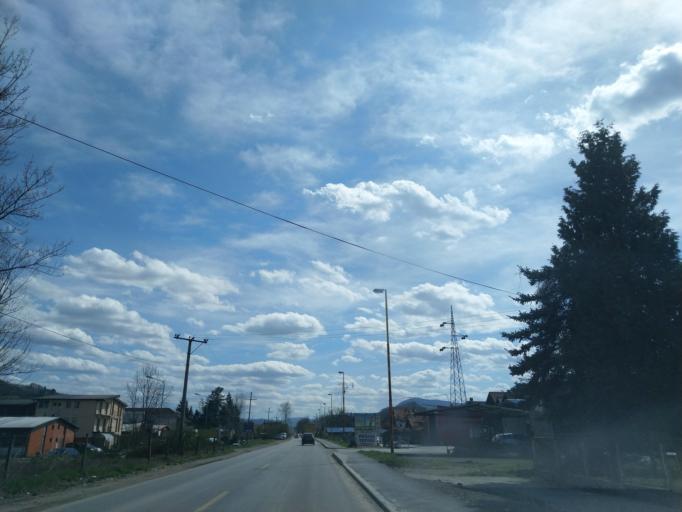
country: RS
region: Central Serbia
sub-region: Zlatiborski Okrug
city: Arilje
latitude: 43.7516
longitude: 20.1047
